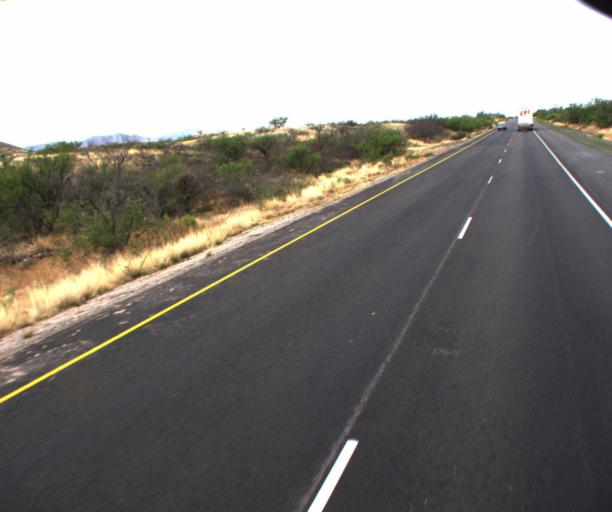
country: US
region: Arizona
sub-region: Cochise County
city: Mescal
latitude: 31.9724
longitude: -110.4843
